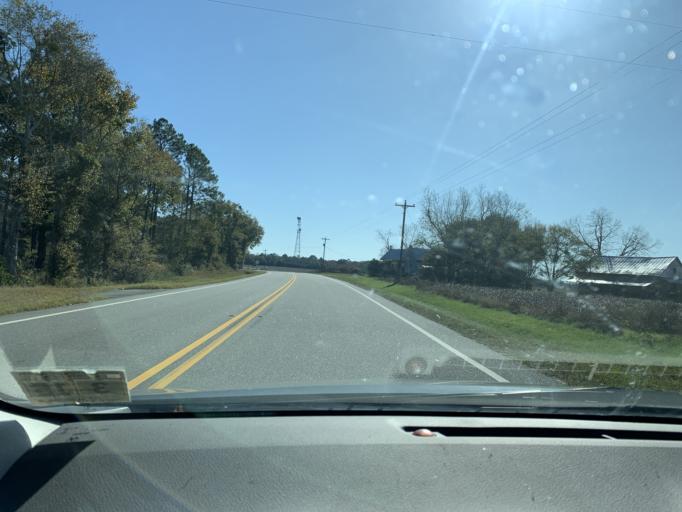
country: US
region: Georgia
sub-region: Ben Hill County
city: Fitzgerald
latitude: 31.7099
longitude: -83.1669
